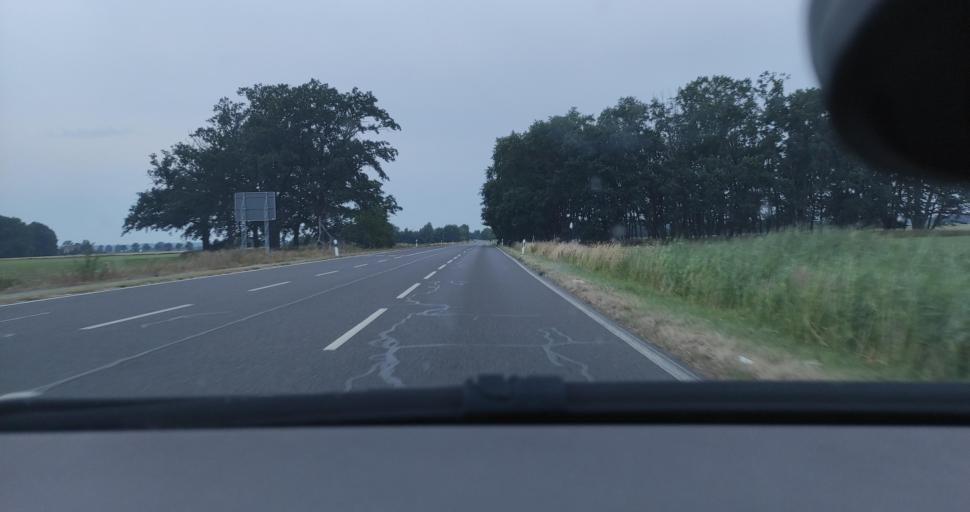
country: DE
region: Brandenburg
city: Forst
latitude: 51.7670
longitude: 14.6457
